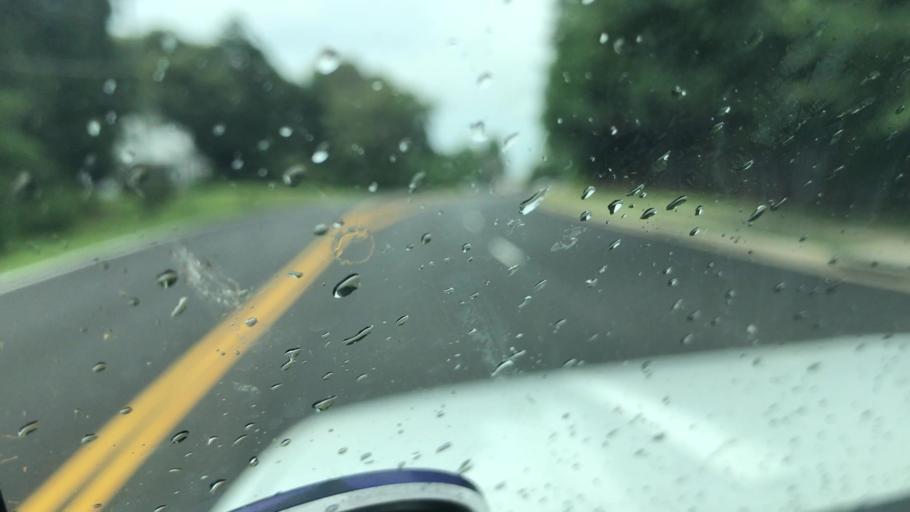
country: US
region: Virginia
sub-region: Henrico County
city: Short Pump
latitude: 37.6443
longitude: -77.6164
